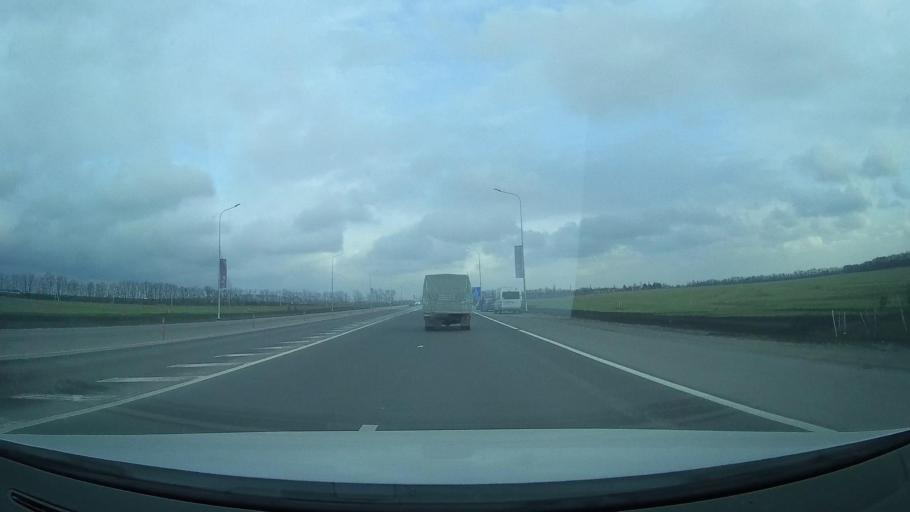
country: RU
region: Rostov
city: Grushevskaya
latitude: 47.4772
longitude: 39.9171
